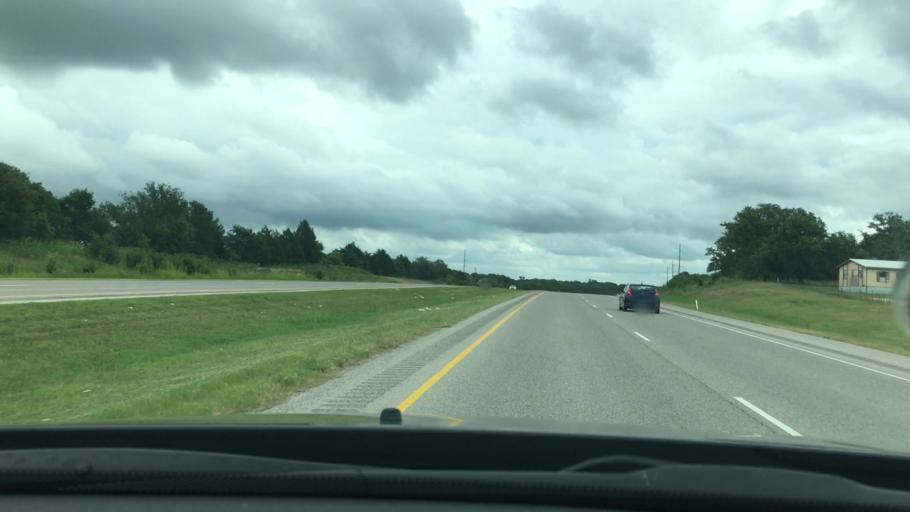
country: US
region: Oklahoma
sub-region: Carter County
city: Ardmore
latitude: 34.1334
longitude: -97.0953
